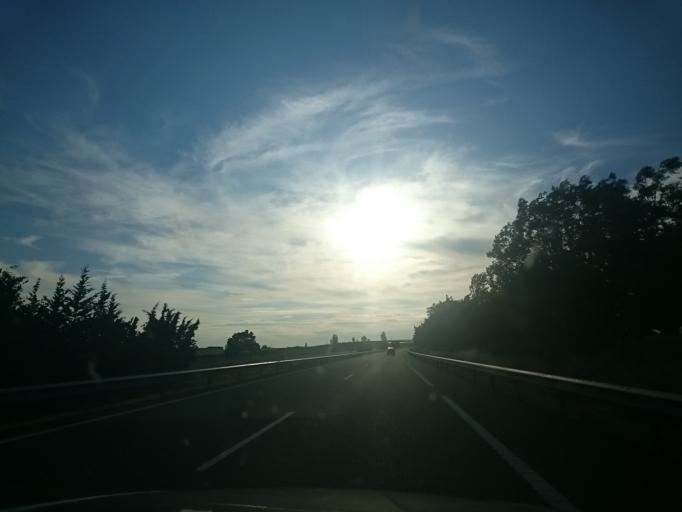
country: ES
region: Castille and Leon
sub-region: Provincia de Leon
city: Sahagun
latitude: 42.3764
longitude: -5.0047
